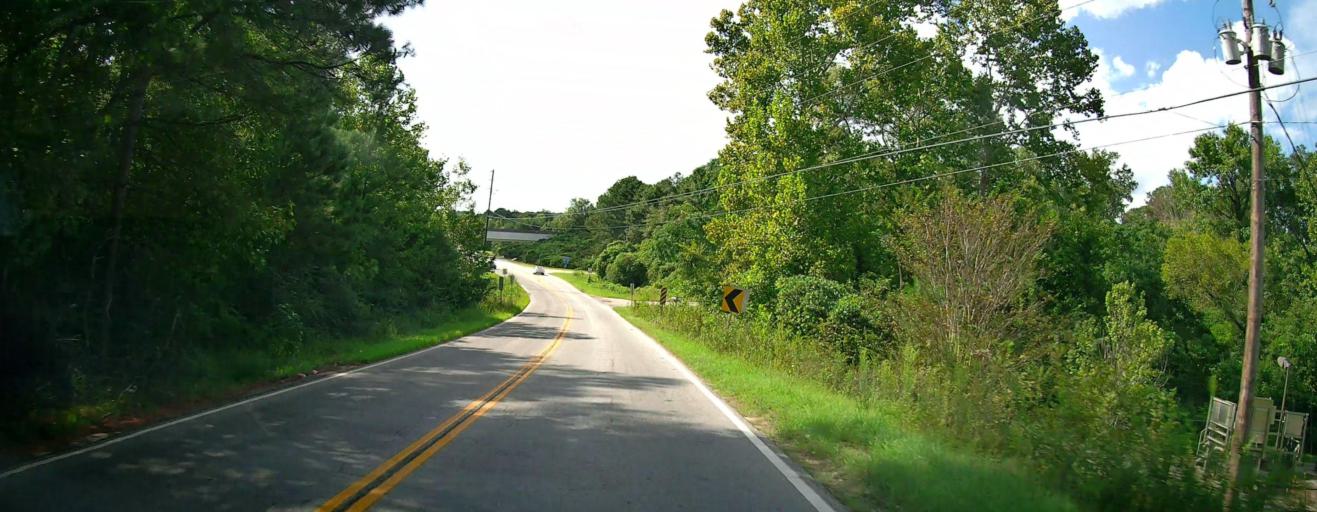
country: US
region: Alabama
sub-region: Russell County
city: Phenix City
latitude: 32.6025
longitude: -84.9492
